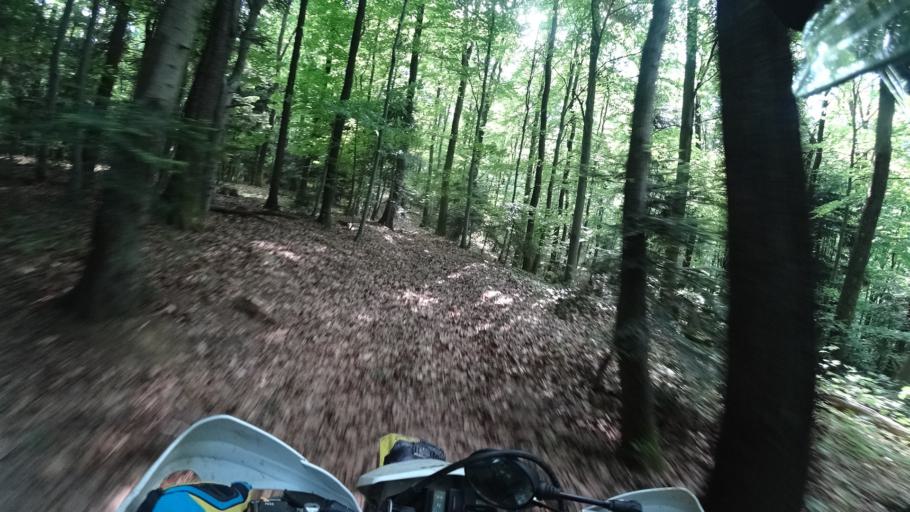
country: HR
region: Grad Zagreb
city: Kasina
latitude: 45.9368
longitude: 15.9414
